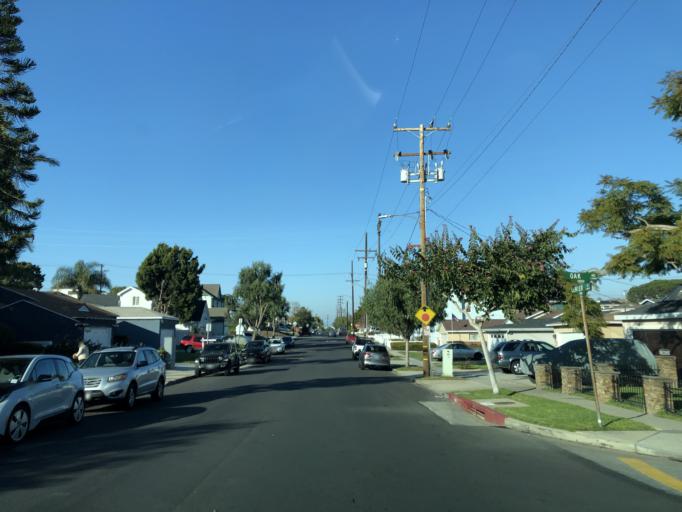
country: US
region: California
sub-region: Los Angeles County
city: El Segundo
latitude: 33.9260
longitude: -118.4049
